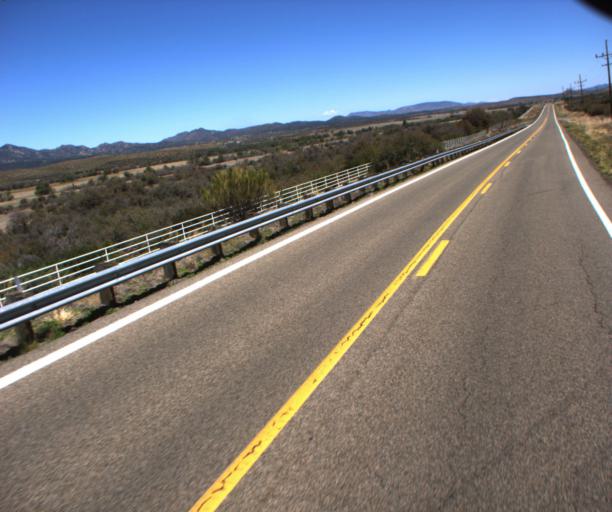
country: US
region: Arizona
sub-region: Yavapai County
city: Congress
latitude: 34.2459
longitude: -112.7364
